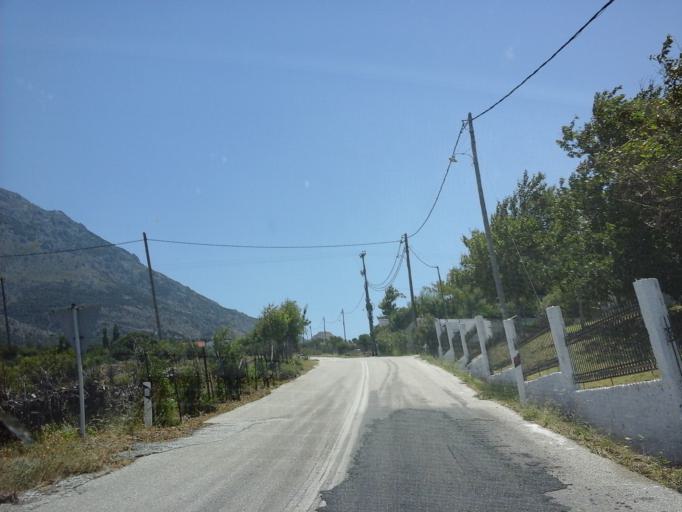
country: GR
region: East Macedonia and Thrace
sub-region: Nomos Evrou
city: Samothraki
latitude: 40.5038
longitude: 25.5237
